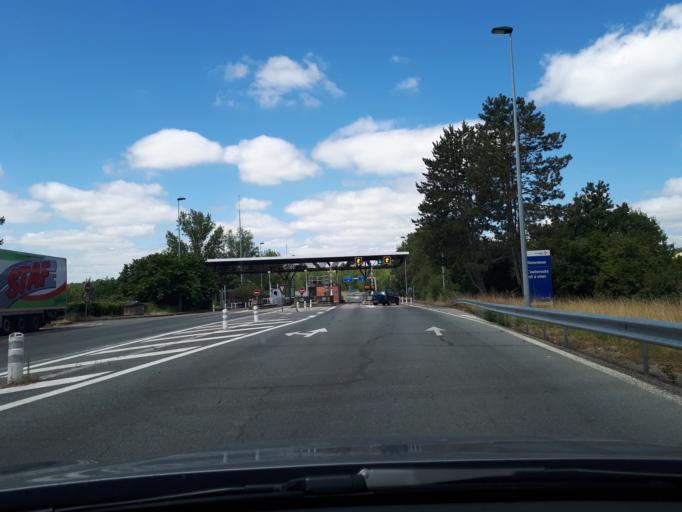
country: FR
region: Midi-Pyrenees
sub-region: Departement du Tarn-et-Garonne
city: Auvillar
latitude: 44.0644
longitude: 0.8676
